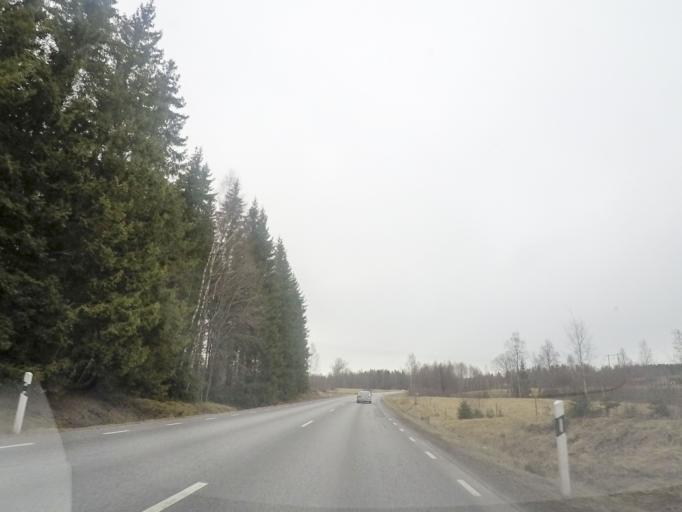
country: SE
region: Vaestmanland
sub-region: Skinnskattebergs Kommun
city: Skinnskatteberg
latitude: 59.8649
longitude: 15.6518
